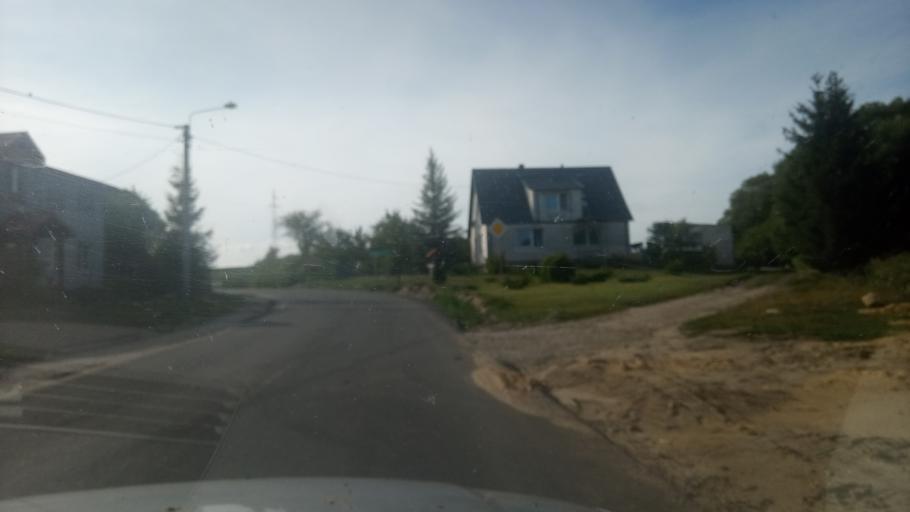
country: PL
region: Kujawsko-Pomorskie
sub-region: Powiat nakielski
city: Sadki
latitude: 53.1964
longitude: 17.3871
